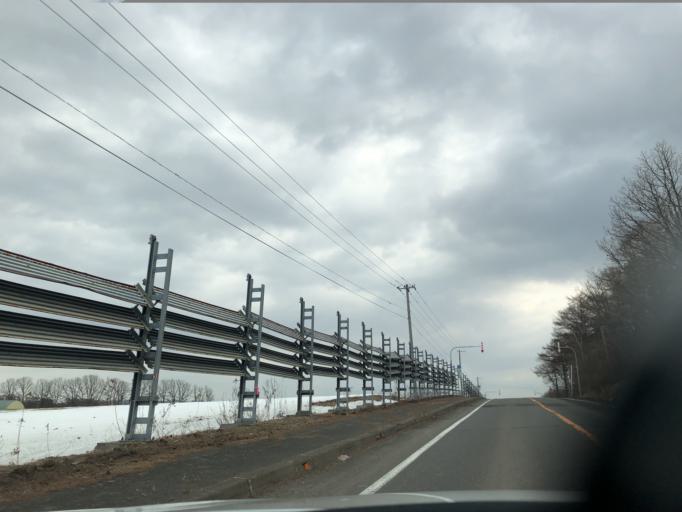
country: JP
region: Hokkaido
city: Chitose
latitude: 42.7601
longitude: 141.7440
